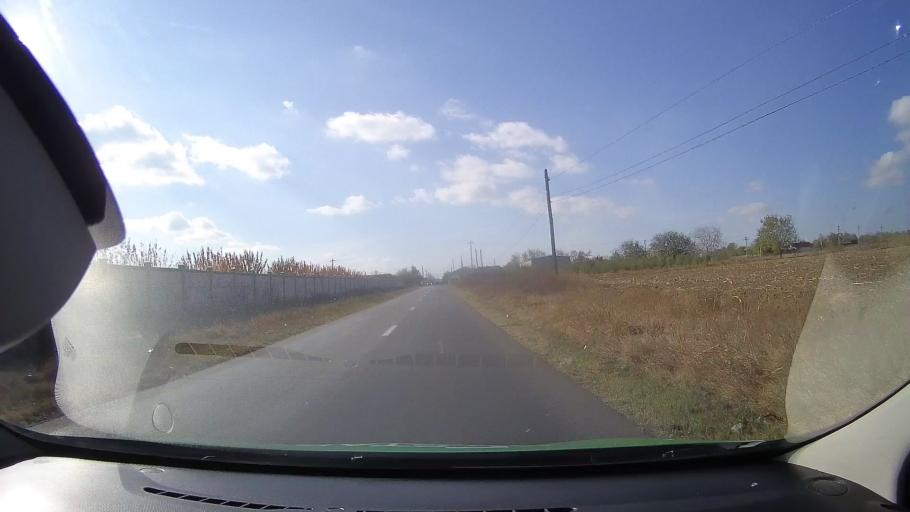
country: RO
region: Constanta
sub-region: Comuna Cogealac
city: Cogealac
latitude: 44.5602
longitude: 28.5738
